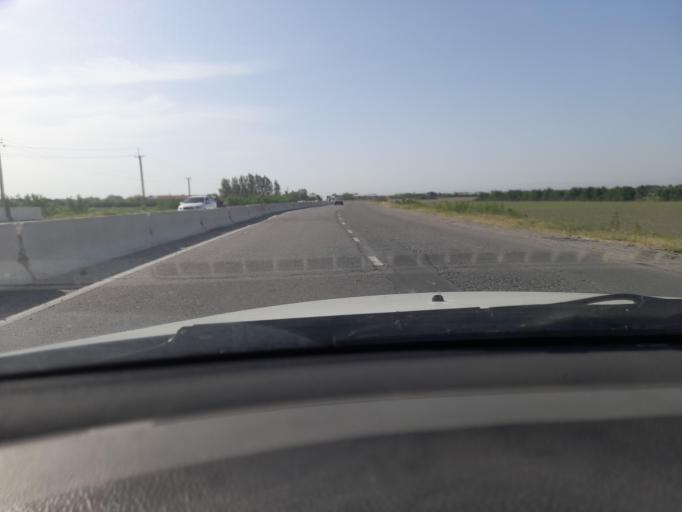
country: UZ
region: Samarqand
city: Kattaqo'rg'on
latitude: 39.9253
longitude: 66.2739
